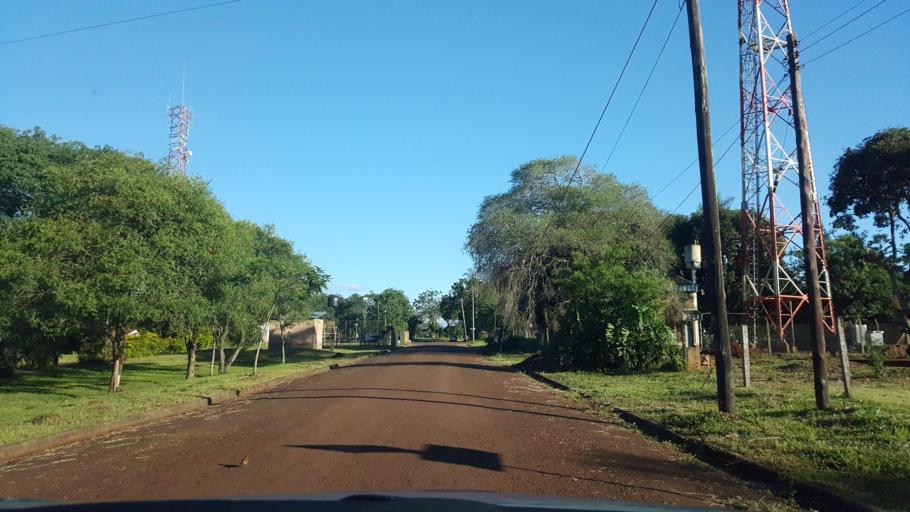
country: AR
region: Misiones
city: Gobernador Roca
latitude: -27.1280
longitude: -55.5128
